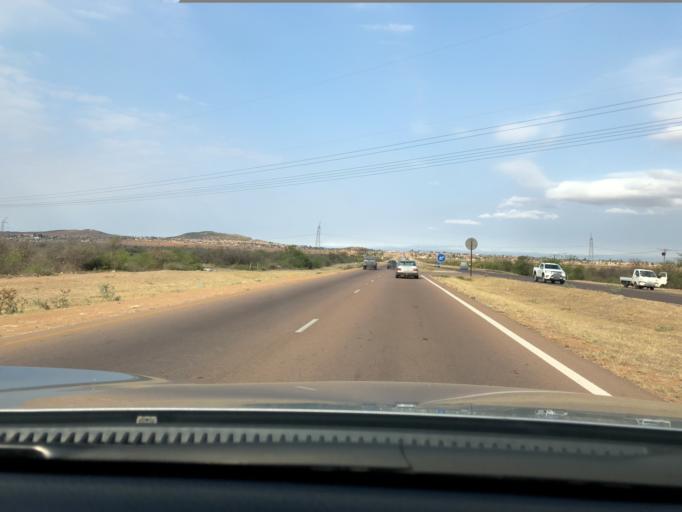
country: ZA
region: Limpopo
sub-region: Capricorn District Municipality
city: Polokwane
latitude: -23.8953
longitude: 29.6332
